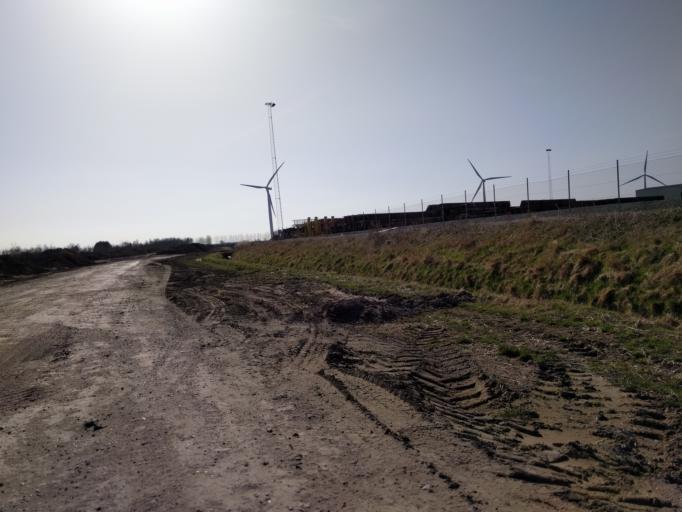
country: DK
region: South Denmark
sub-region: Kerteminde Kommune
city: Munkebo
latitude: 55.4605
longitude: 10.5271
